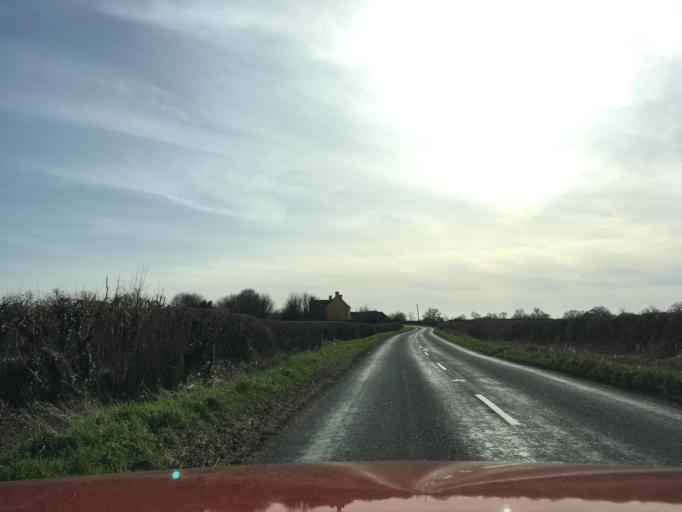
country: GB
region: England
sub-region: Wiltshire
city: Luckington
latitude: 51.5403
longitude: -2.2551
